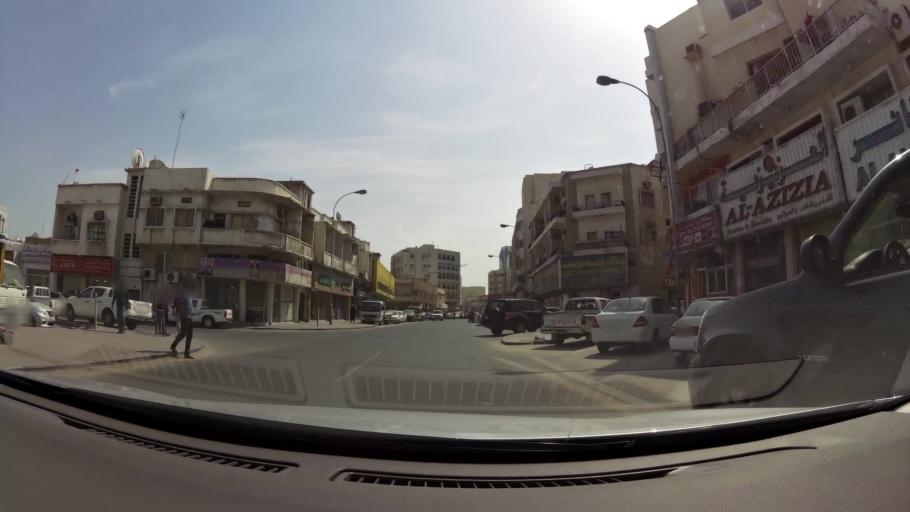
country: QA
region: Baladiyat ad Dawhah
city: Doha
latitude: 25.2826
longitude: 51.5325
